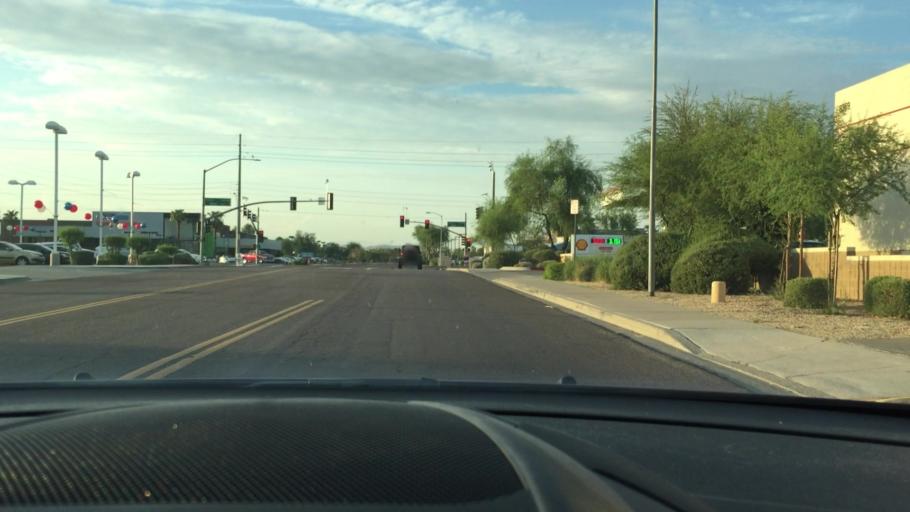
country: US
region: Arizona
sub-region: Maricopa County
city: Sun City
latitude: 33.6372
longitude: -112.2420
